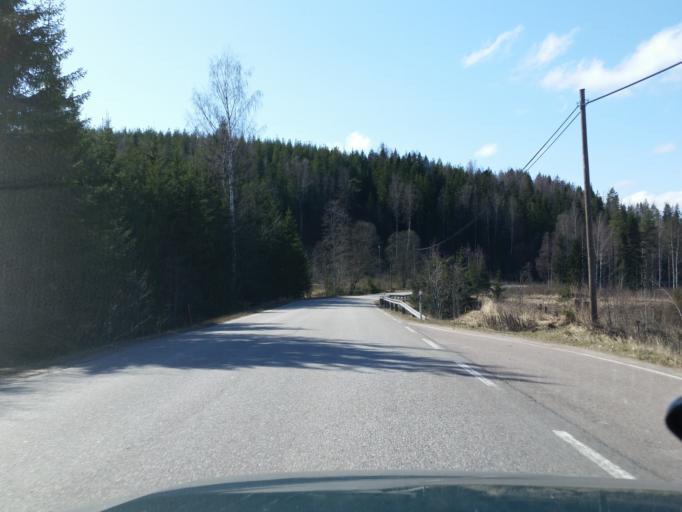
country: FI
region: Uusimaa
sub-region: Helsinki
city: Vihti
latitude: 60.4251
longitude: 24.2609
